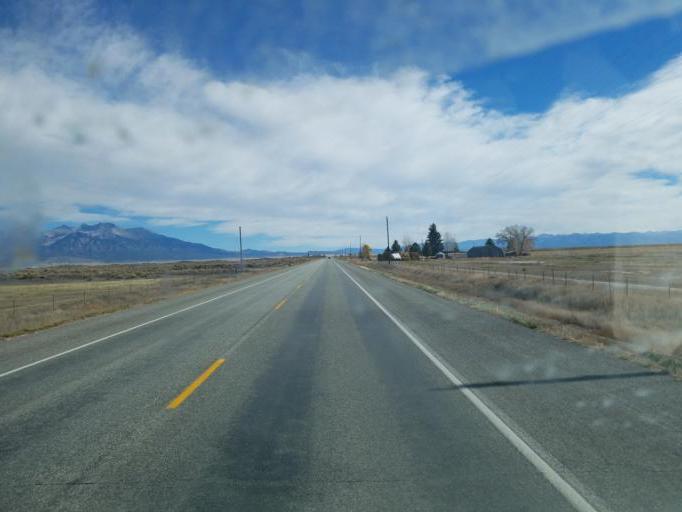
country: US
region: Colorado
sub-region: Alamosa County
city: Alamosa East
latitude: 37.4739
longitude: -105.7599
